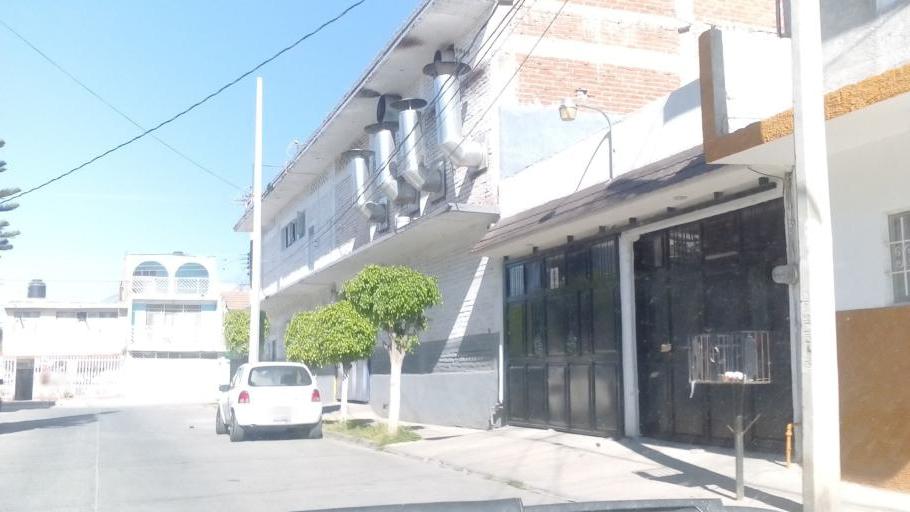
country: MX
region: Guanajuato
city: Leon
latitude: 21.1456
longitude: -101.6748
